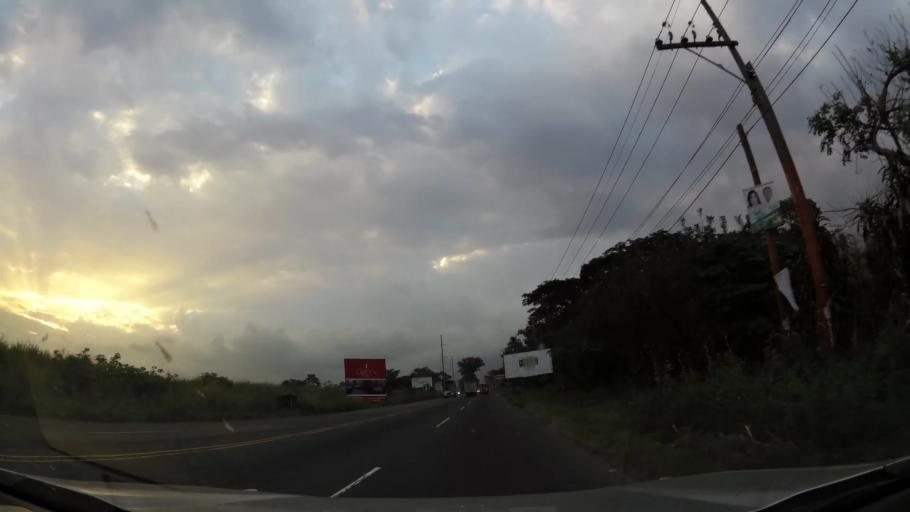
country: GT
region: Escuintla
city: Siquinala
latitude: 14.2948
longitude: -90.9452
